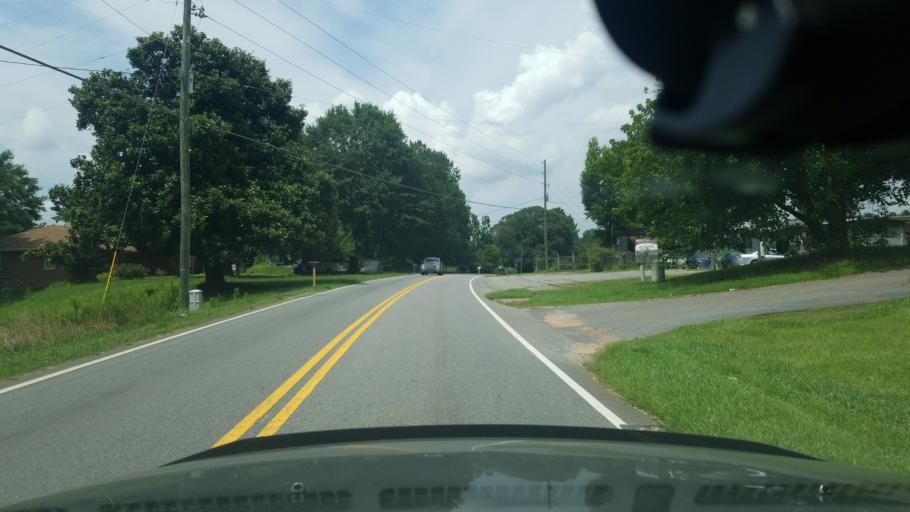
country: US
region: Georgia
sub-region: Forsyth County
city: Cumming
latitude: 34.2643
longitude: -84.2379
